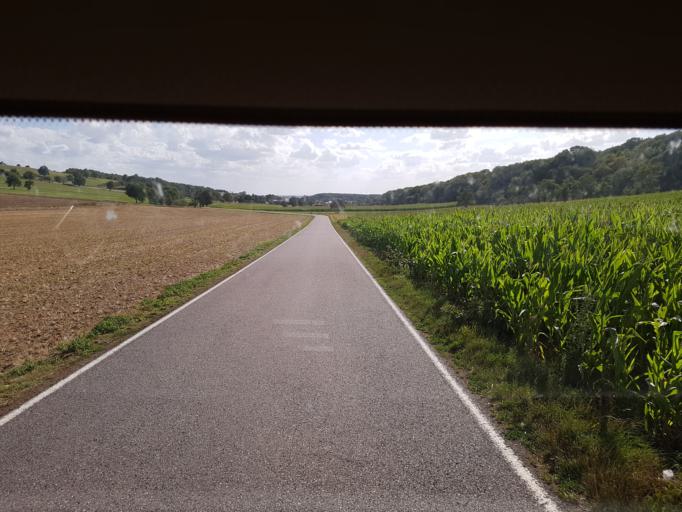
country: DE
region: Rheinland-Pfalz
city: Kirf
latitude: 49.5404
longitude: 6.4435
